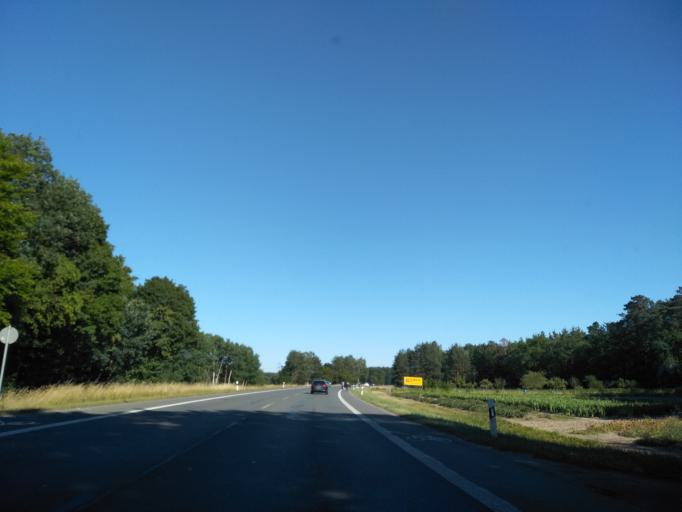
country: DE
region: Bavaria
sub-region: Regierungsbezirk Mittelfranken
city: Hessdorf
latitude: 49.6241
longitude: 10.9455
